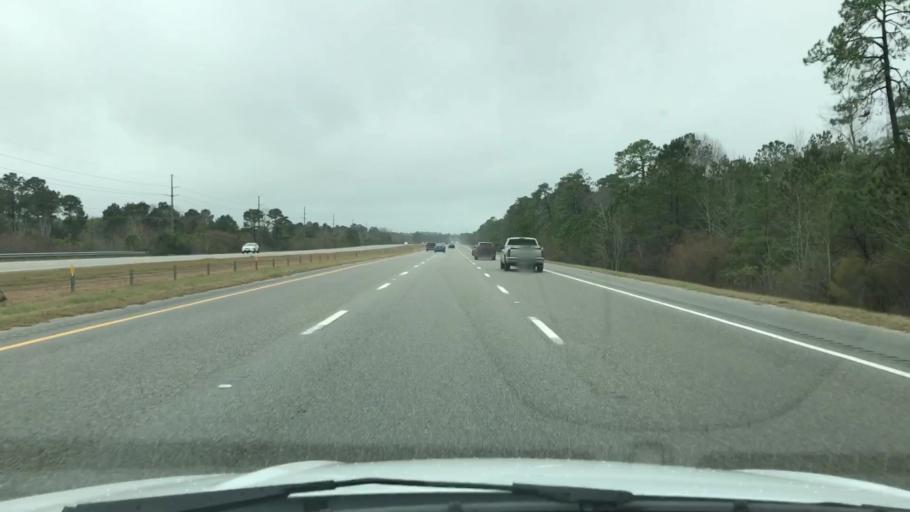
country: US
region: South Carolina
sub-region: Horry County
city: Forestbrook
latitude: 33.7466
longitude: -78.9150
